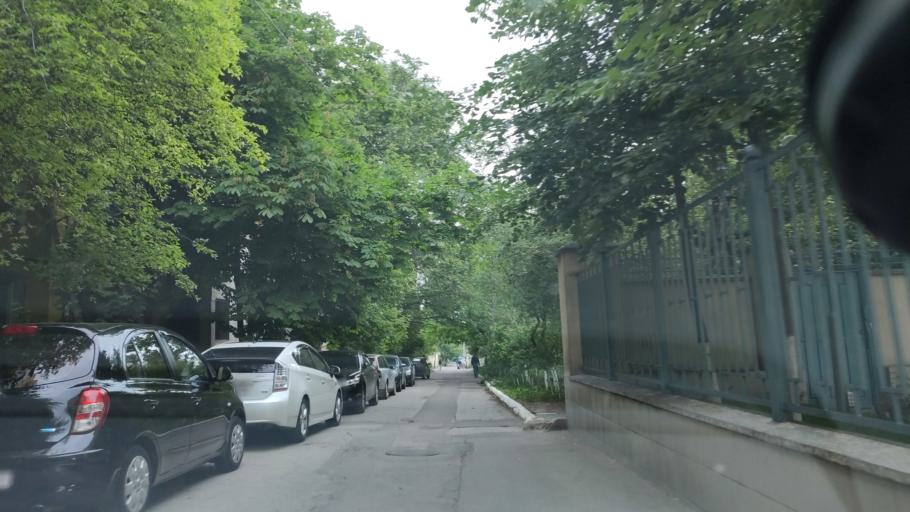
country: MD
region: Chisinau
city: Chisinau
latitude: 46.9831
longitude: 28.8703
